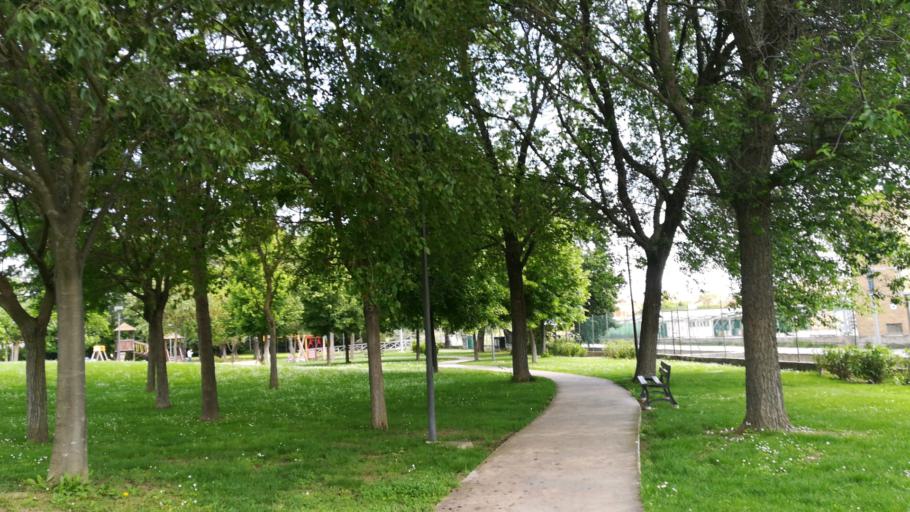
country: IT
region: The Marches
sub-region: Provincia di Macerata
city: Borgo Stazione
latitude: 43.2803
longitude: 13.6412
